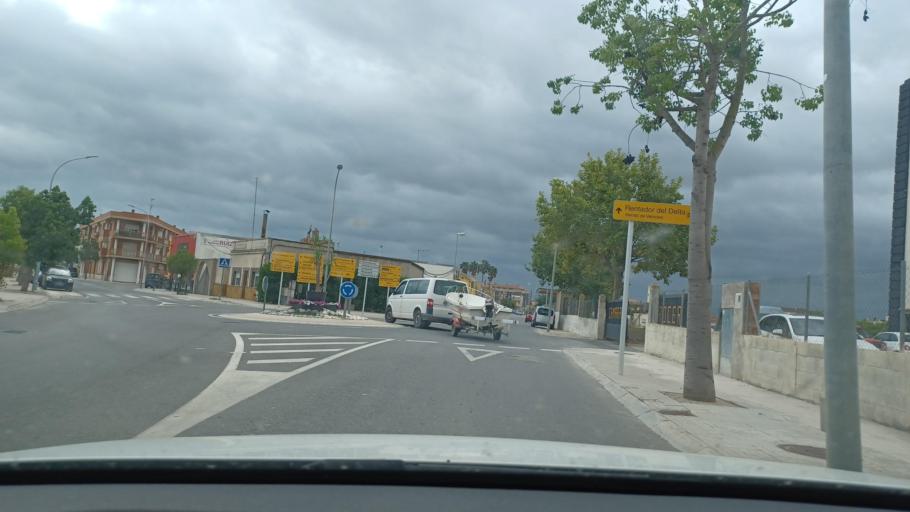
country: ES
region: Catalonia
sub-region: Provincia de Tarragona
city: Deltebre
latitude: 40.7228
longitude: 0.7251
